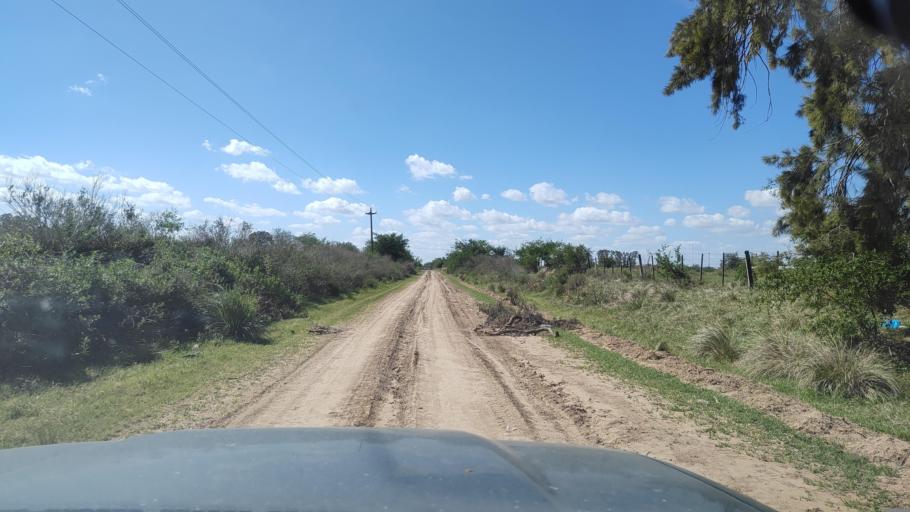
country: AR
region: Buenos Aires
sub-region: Partido de Lujan
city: Lujan
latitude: -34.5230
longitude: -59.1571
